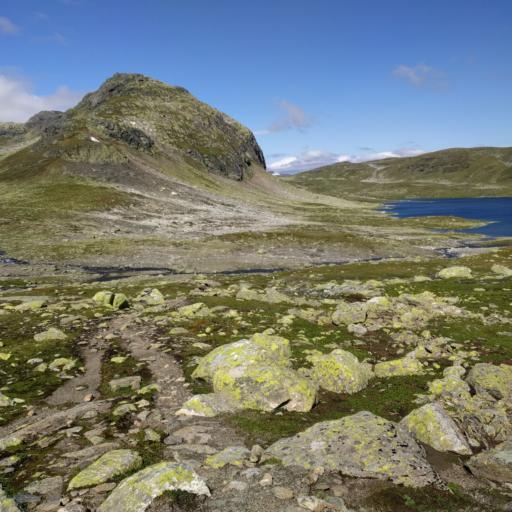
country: NO
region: Aust-Agder
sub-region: Bykle
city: Hovden
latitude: 59.8671
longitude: 7.2161
